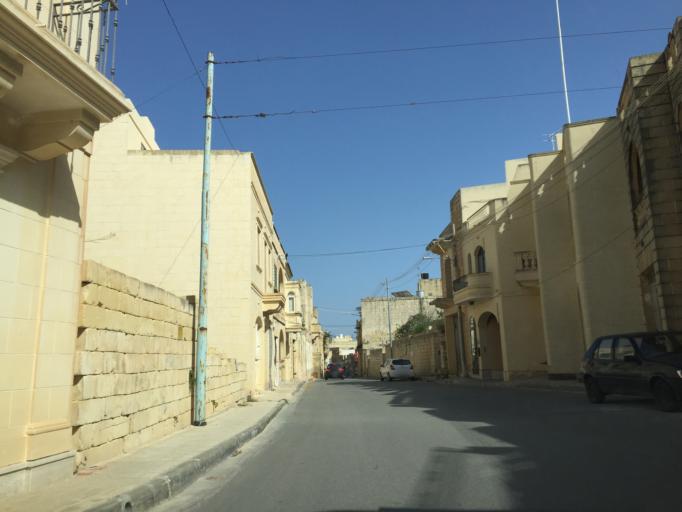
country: MT
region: L-Gharb
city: Gharb
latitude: 36.0568
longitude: 14.2120
